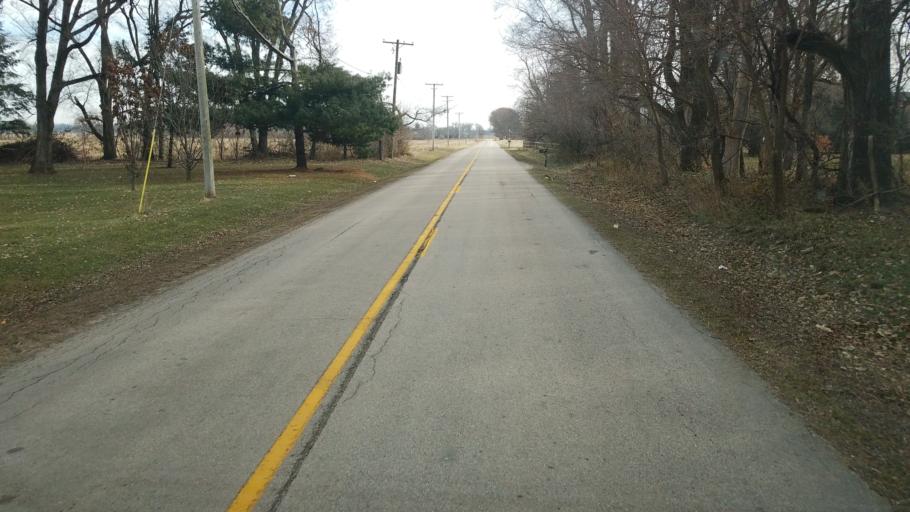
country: US
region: Illinois
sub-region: McHenry County
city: Marengo
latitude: 42.2375
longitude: -88.6509
